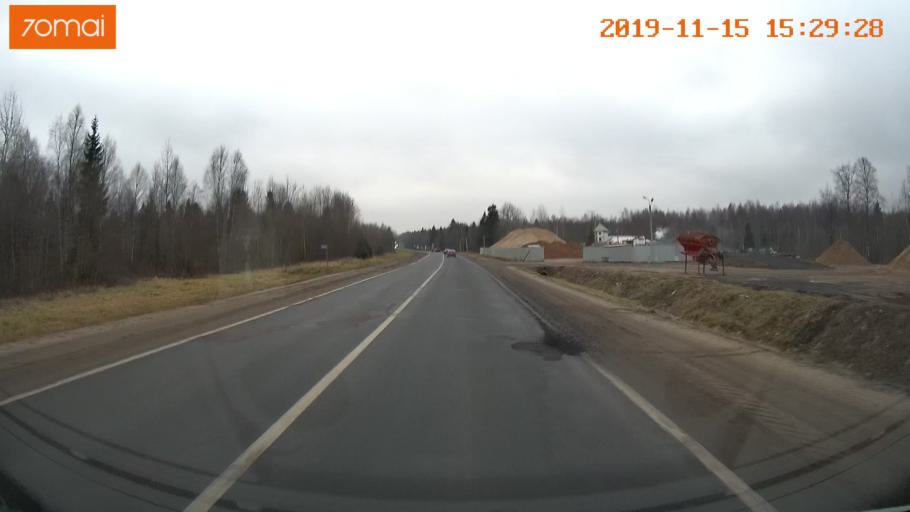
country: RU
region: Jaroslavl
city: Danilov
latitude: 58.1204
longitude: 40.1198
